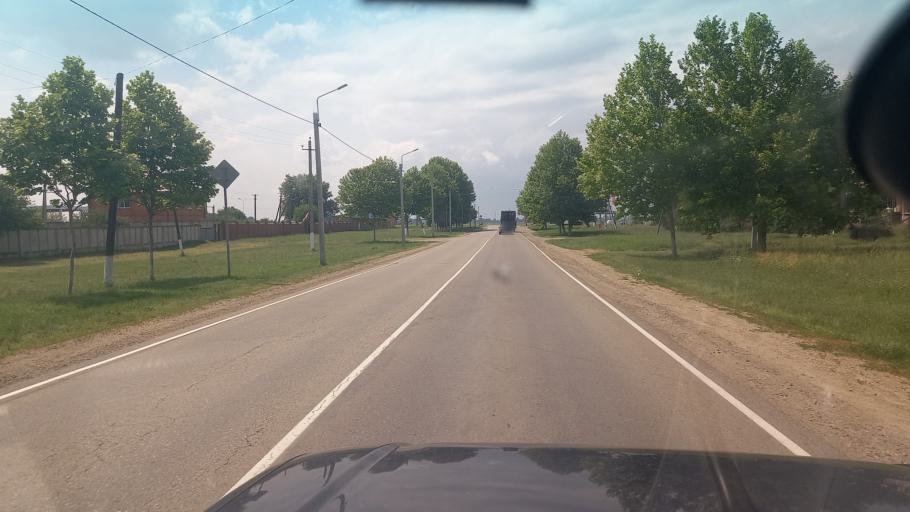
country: RU
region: Adygeya
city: Koshekhabl'
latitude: 44.9010
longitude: 40.4777
